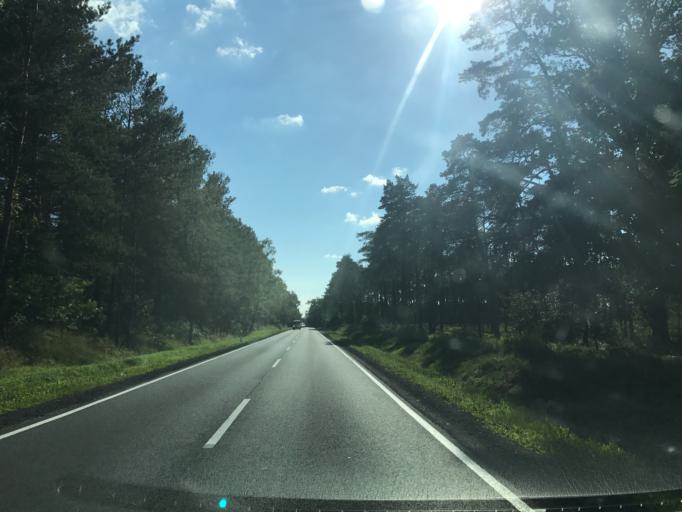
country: PL
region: Kujawsko-Pomorskie
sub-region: Wloclawek
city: Wloclawek
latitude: 52.6283
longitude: 19.0017
